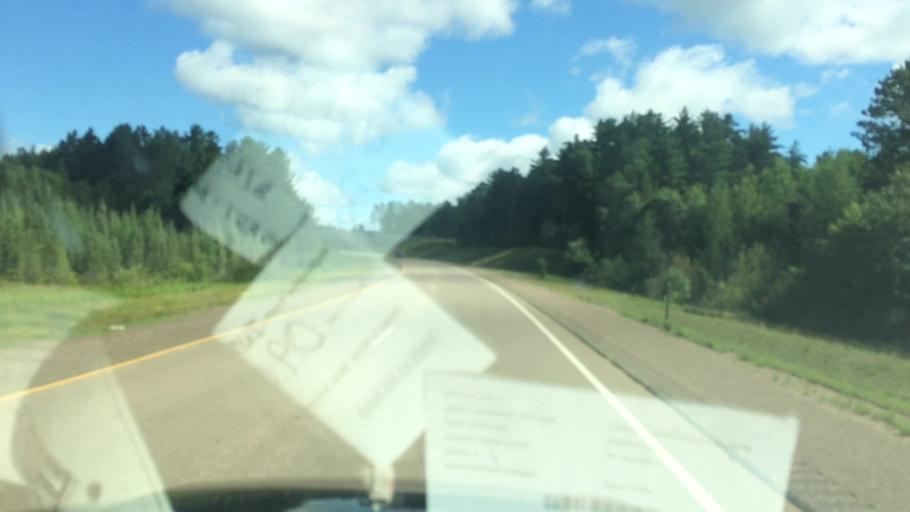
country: US
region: Wisconsin
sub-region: Lincoln County
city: Tomahawk
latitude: 45.5179
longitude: -89.6754
